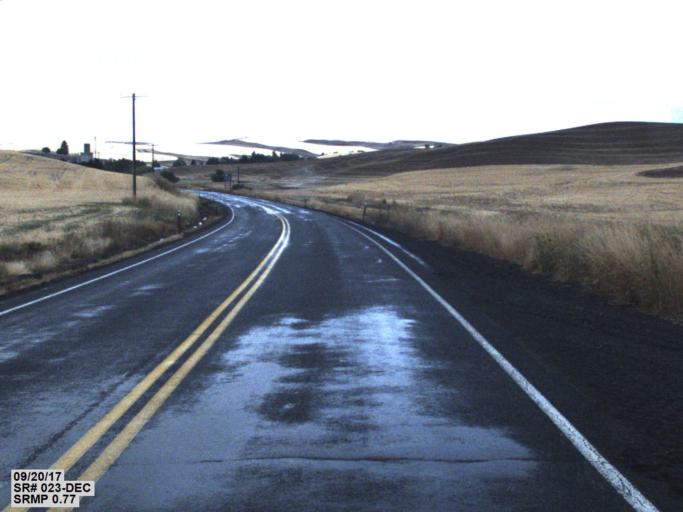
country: US
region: Washington
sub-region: Whitman County
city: Colfax
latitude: 47.0033
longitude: -117.3696
